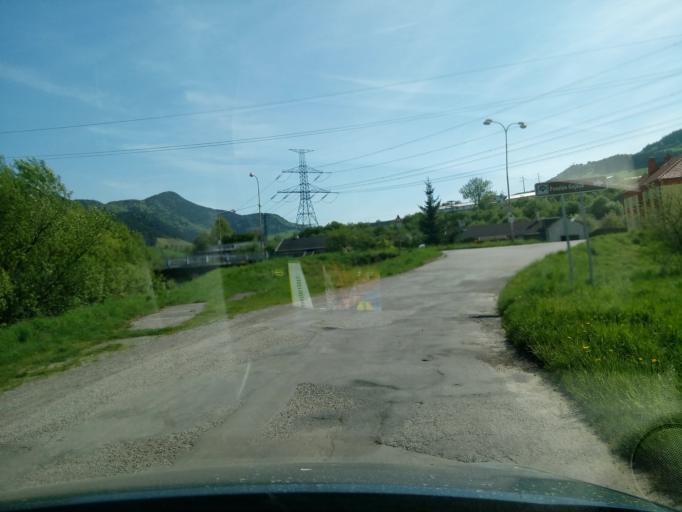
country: SK
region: Zilinsky
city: Ruzomberok
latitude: 49.0600
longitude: 19.3033
